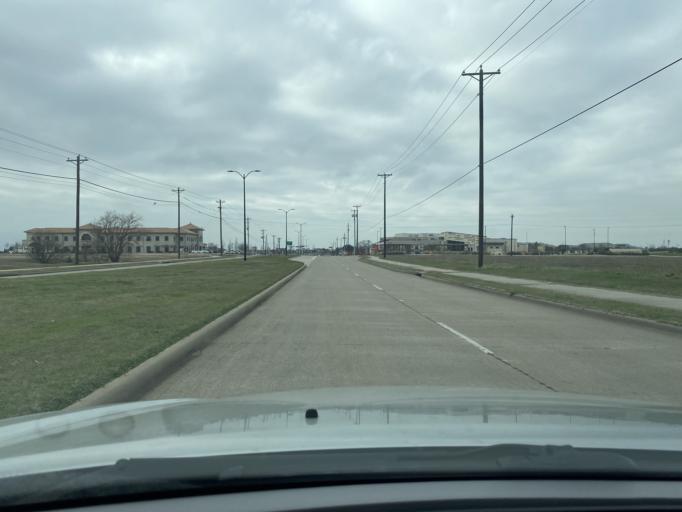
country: US
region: Texas
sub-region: Collin County
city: Frisco
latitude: 33.1237
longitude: -96.8125
